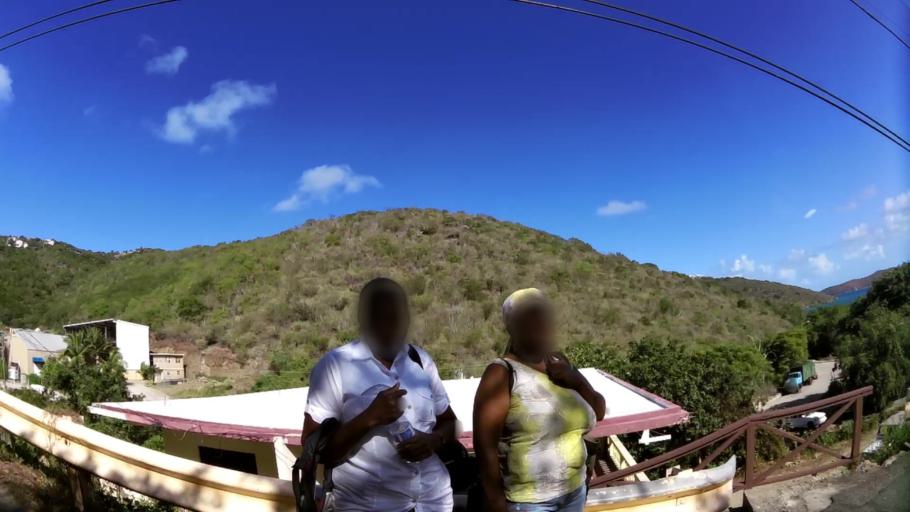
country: VG
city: Tortola
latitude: 18.4880
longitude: -64.3835
